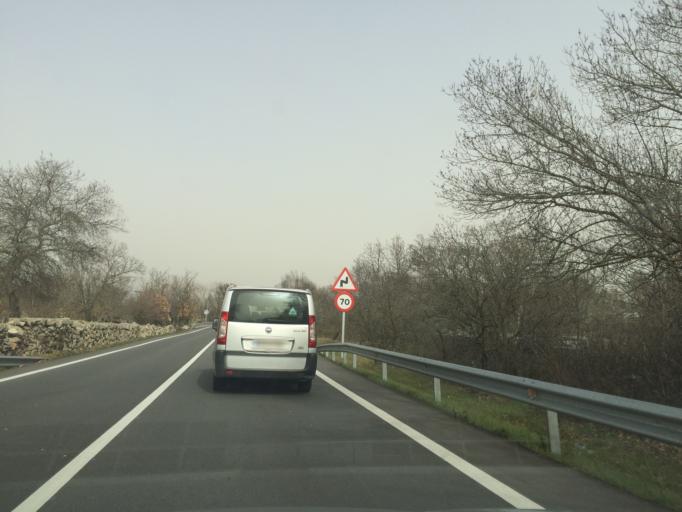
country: ES
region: Madrid
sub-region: Provincia de Madrid
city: Moralzarzal
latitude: 40.6906
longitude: -3.9465
